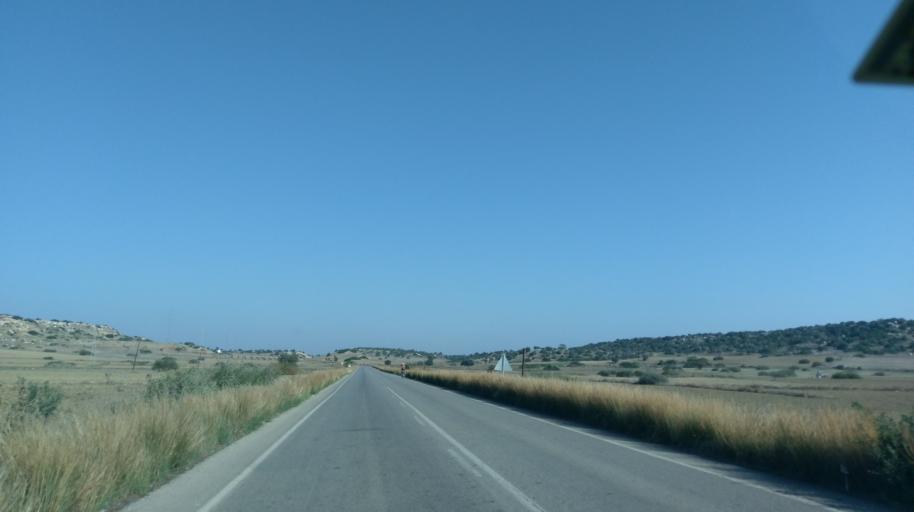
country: CY
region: Ammochostos
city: Leonarisso
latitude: 35.3833
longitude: 34.0460
